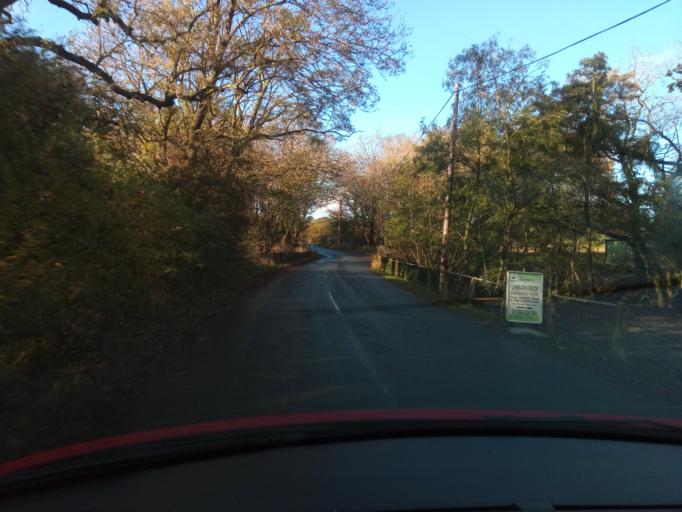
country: GB
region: England
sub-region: County Durham
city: Hamsterley
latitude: 54.6663
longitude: -1.8131
